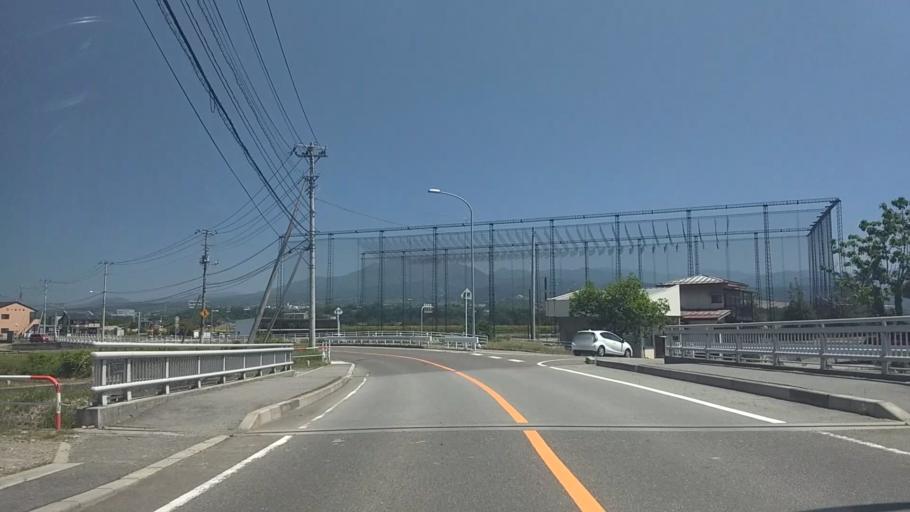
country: JP
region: Yamanashi
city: Nirasaki
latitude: 35.6870
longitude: 138.4617
